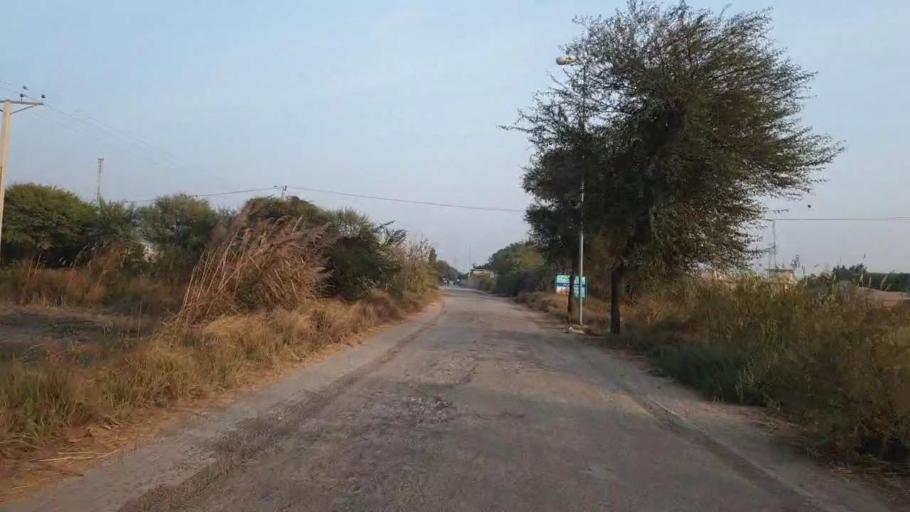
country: PK
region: Sindh
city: Matiari
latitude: 25.6025
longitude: 68.4393
